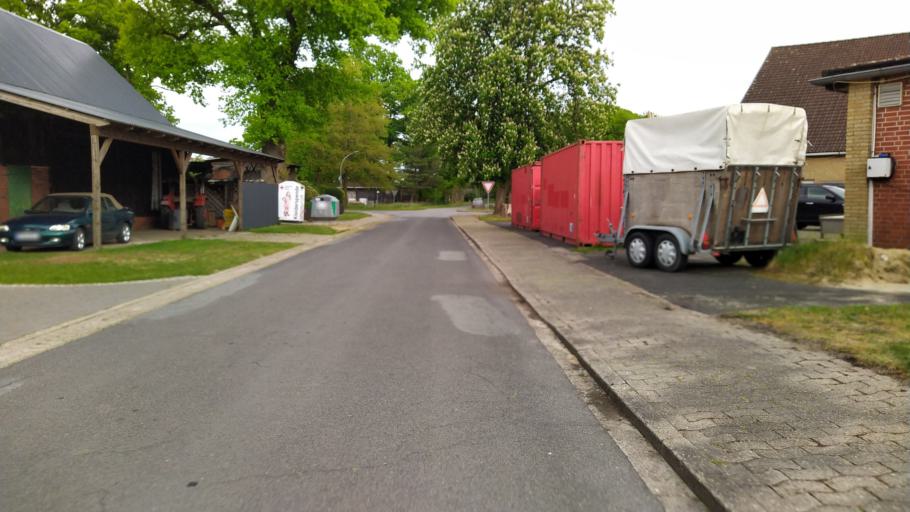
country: DE
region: Lower Saxony
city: Ahlerstedt
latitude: 53.4042
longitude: 9.4082
